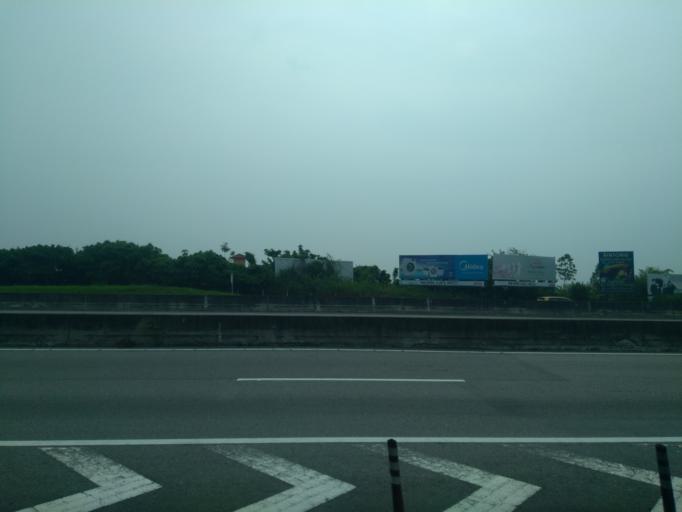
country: MY
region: Perak
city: Ipoh
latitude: 4.5811
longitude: 101.1438
